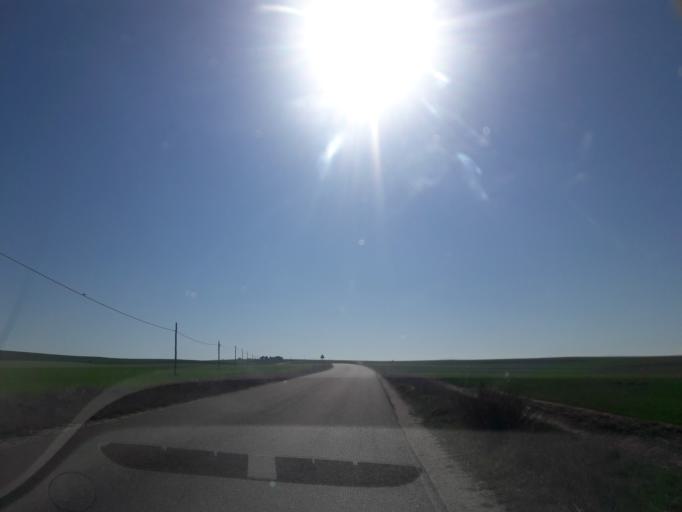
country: ES
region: Castille and Leon
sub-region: Provincia de Salamanca
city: Tordillos
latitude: 40.8505
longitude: -5.3258
